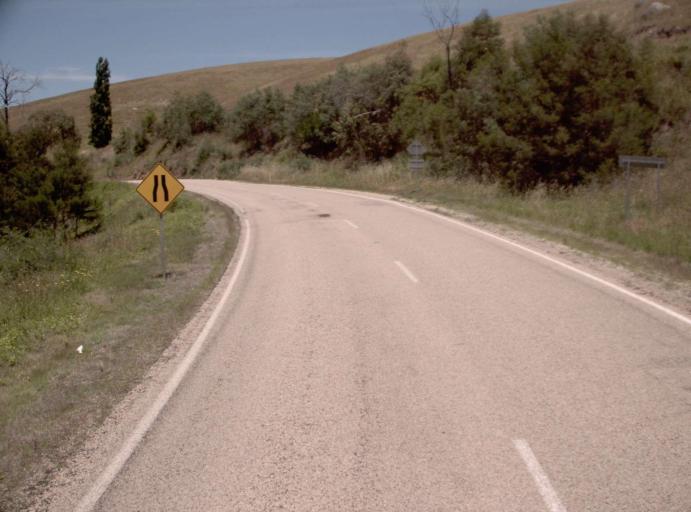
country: AU
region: Victoria
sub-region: East Gippsland
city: Bairnsdale
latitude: -37.5142
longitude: 147.8464
